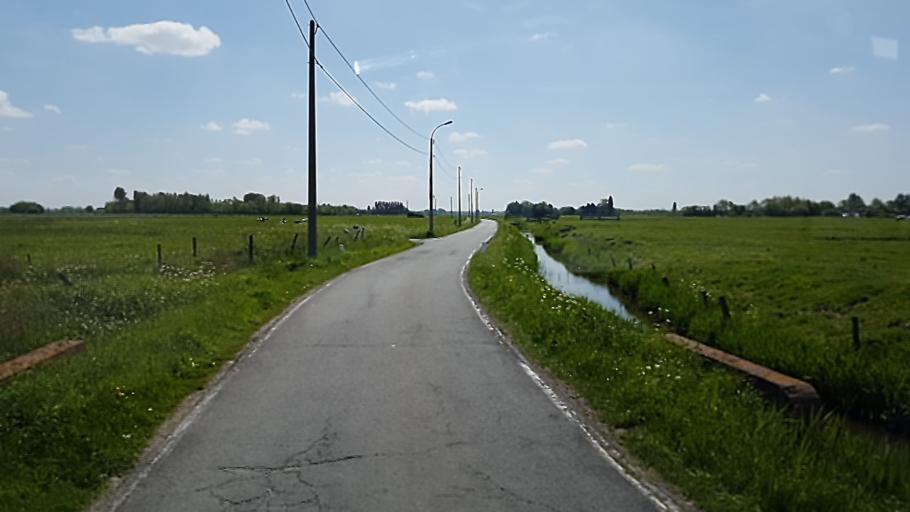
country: BE
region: Flanders
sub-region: Provincie West-Vlaanderen
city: De Haan
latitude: 51.2434
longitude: 3.0468
